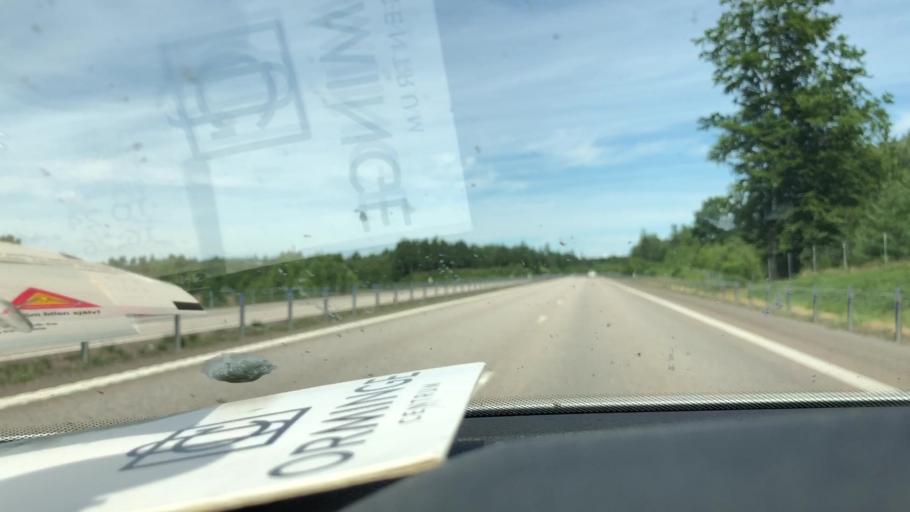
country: SE
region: Skane
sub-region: Orkelljunga Kommun
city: OErkelljunga
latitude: 56.3166
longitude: 13.4164
